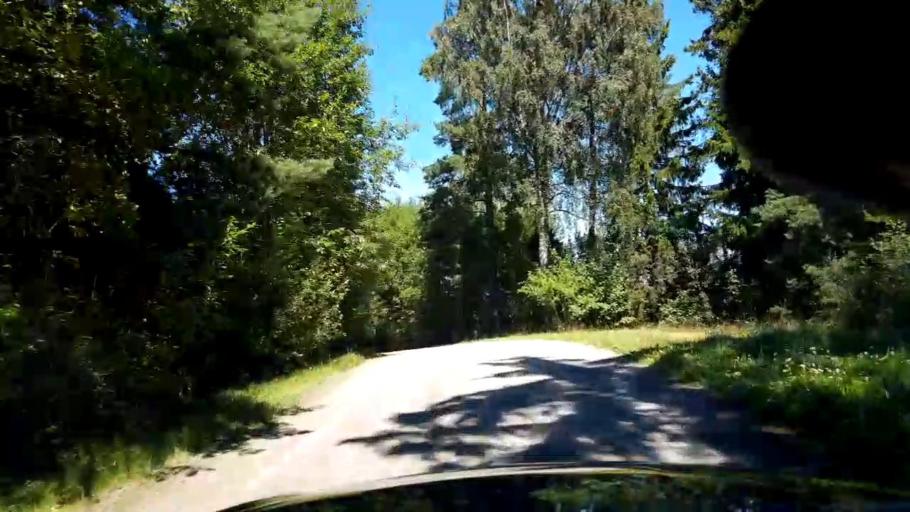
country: SE
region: Uppsala
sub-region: Habo Kommun
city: Balsta
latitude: 59.6169
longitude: 17.6138
